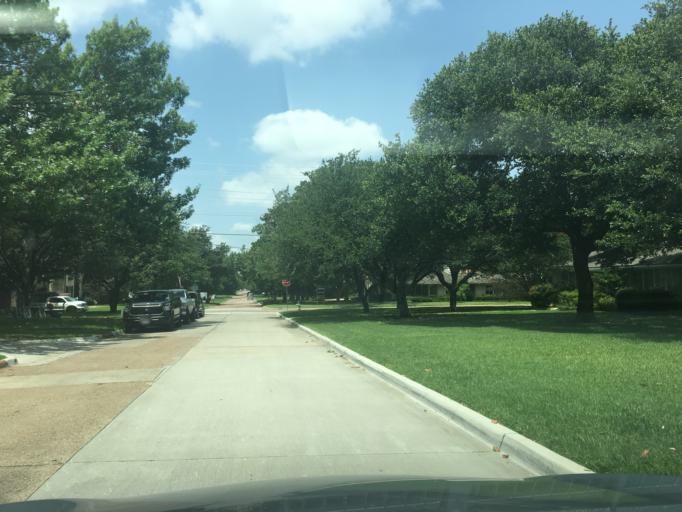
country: US
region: Texas
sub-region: Dallas County
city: University Park
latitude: 32.8781
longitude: -96.7896
